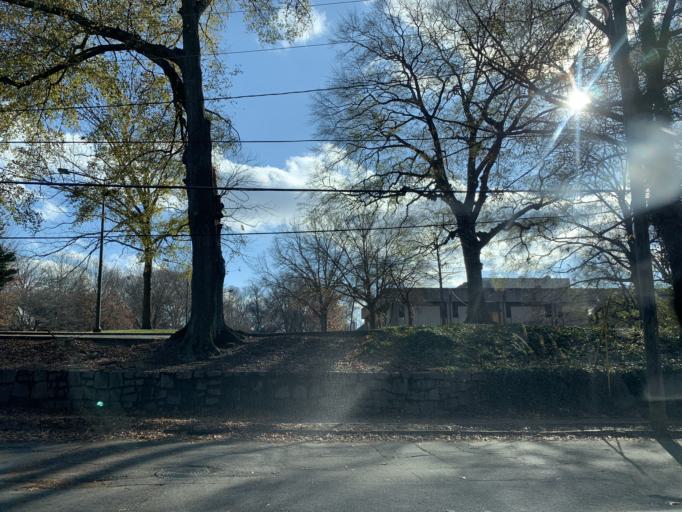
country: US
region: Georgia
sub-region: Fulton County
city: Atlanta
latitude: 33.7379
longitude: -84.3790
